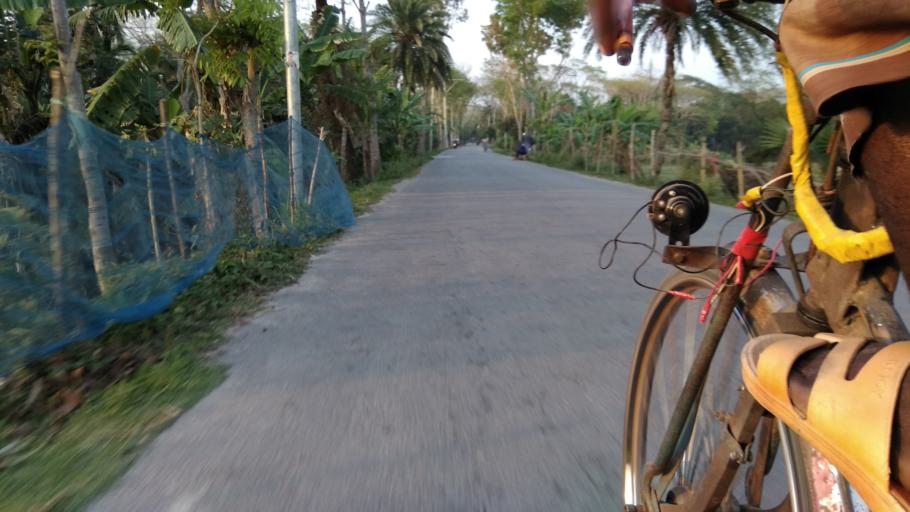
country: BD
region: Barisal
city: Mehendiganj
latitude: 22.9312
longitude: 90.4049
